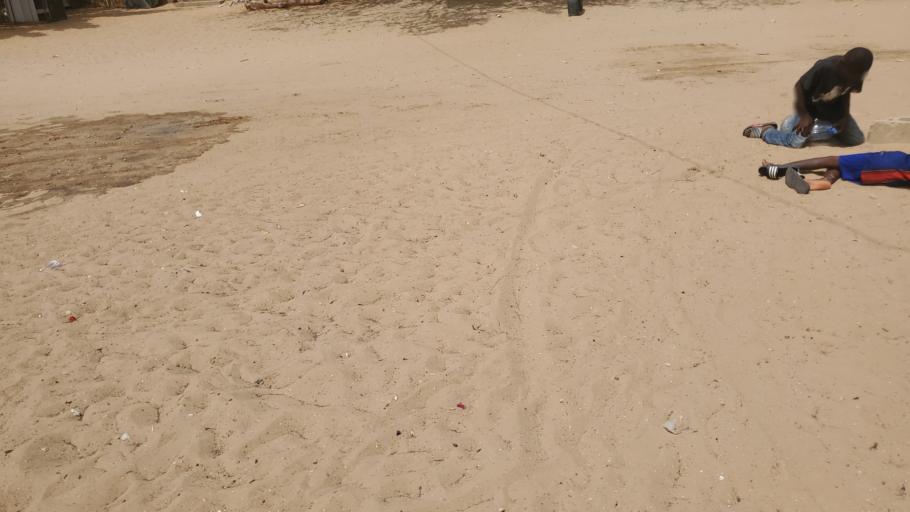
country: SN
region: Saint-Louis
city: Saint-Louis
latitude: 16.0187
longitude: -16.4846
